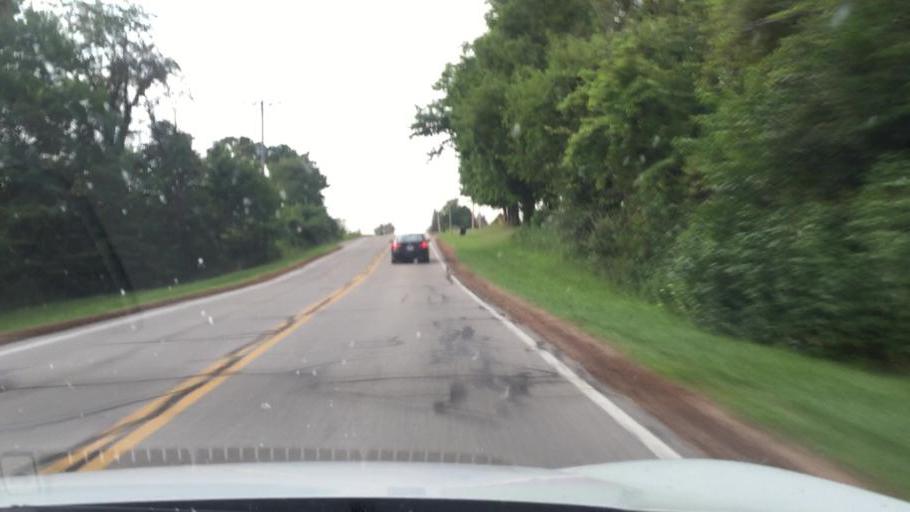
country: US
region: Ohio
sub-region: Champaign County
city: Mechanicsburg
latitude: 40.0456
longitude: -83.5677
